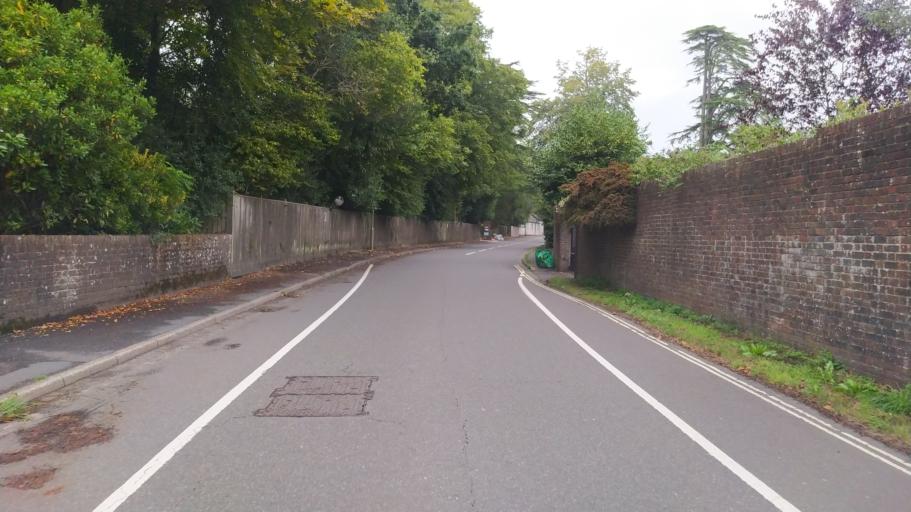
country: GB
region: England
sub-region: Hampshire
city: Lyndhurst
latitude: 50.8698
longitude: -1.5822
